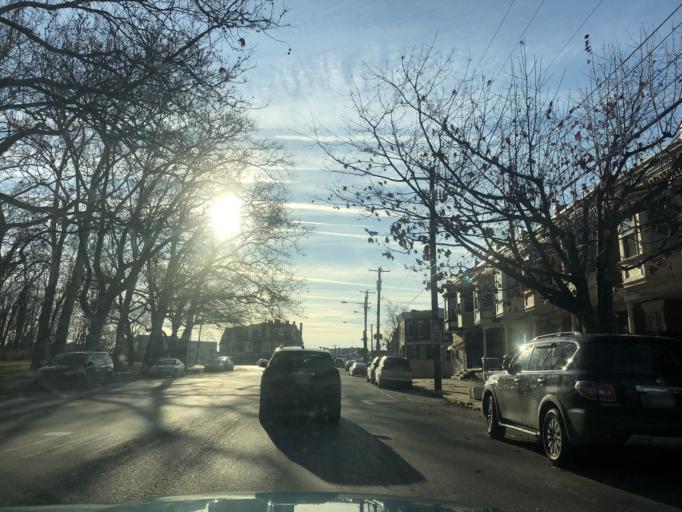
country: US
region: Pennsylvania
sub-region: Montgomery County
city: Bala-Cynwyd
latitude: 39.9825
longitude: -75.2269
